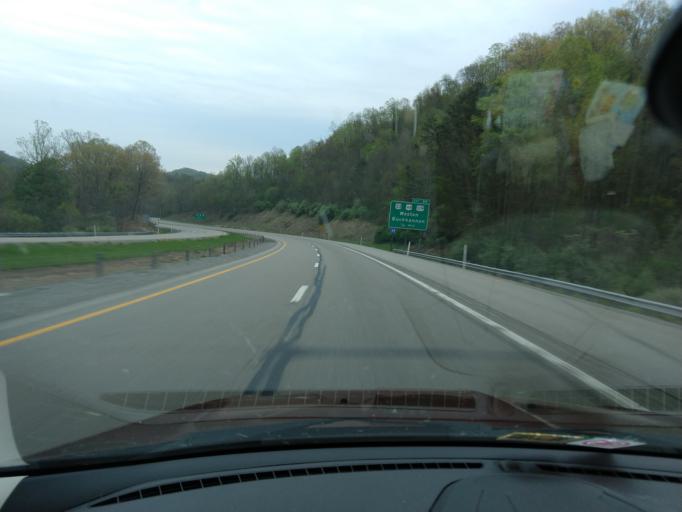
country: US
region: West Virginia
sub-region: Lewis County
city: Weston
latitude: 39.0162
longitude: -80.4349
